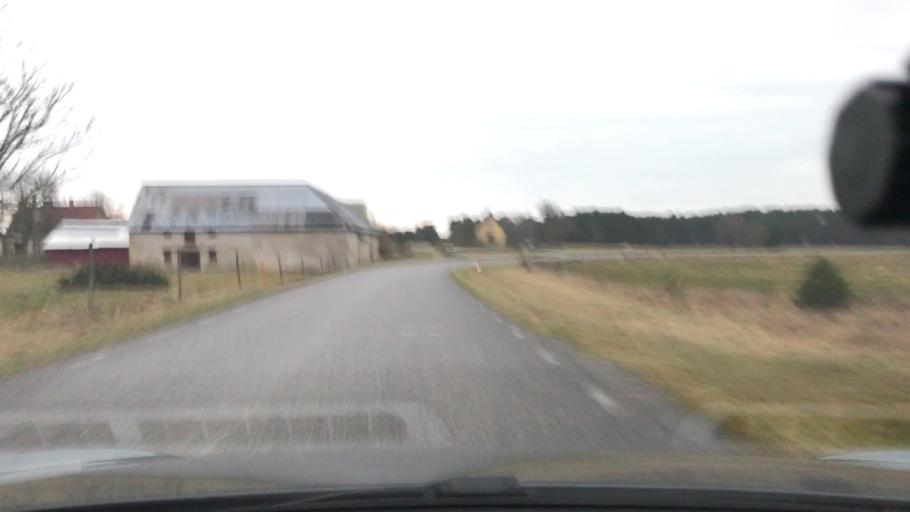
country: SE
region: Gotland
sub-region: Gotland
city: Slite
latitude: 57.3966
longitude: 18.8060
